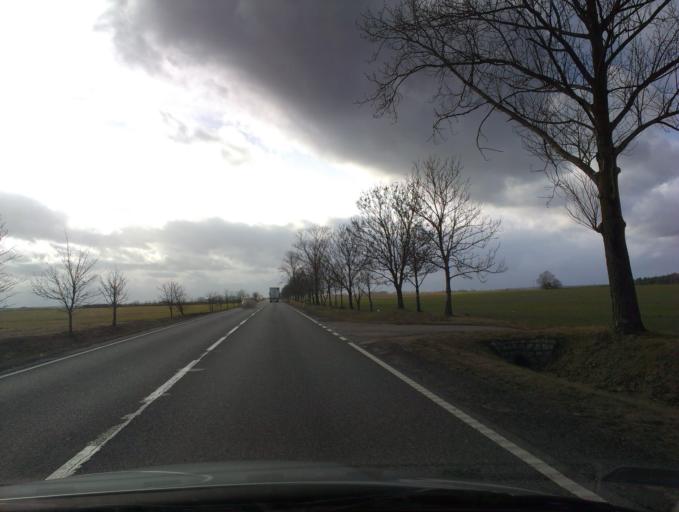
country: PL
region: Pomeranian Voivodeship
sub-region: Powiat czluchowski
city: Debrzno
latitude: 53.6233
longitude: 17.2142
